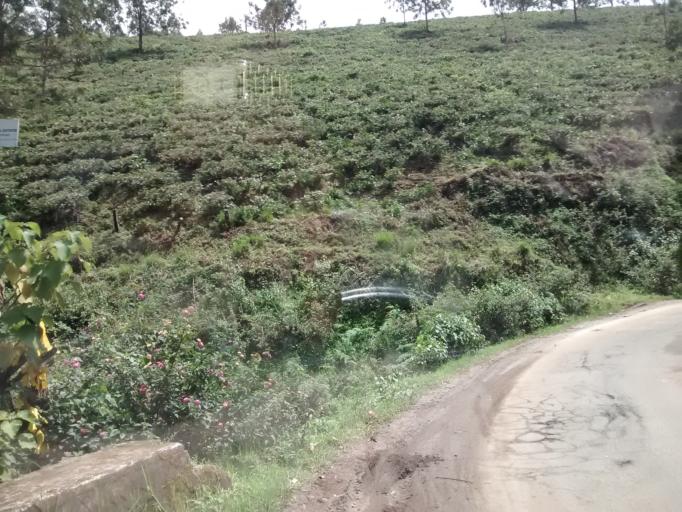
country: IN
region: Kerala
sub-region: Idukki
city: Munnar
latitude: 10.1028
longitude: 77.1121
